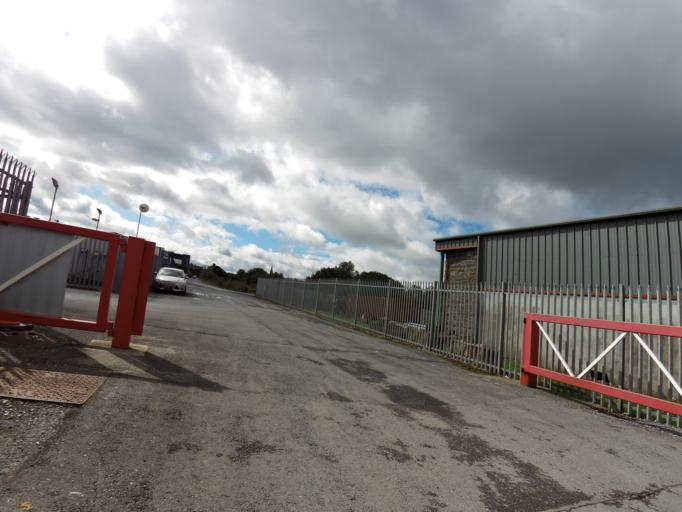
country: IE
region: Connaught
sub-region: County Galway
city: Loughrea
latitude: 53.2028
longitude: -8.5667
